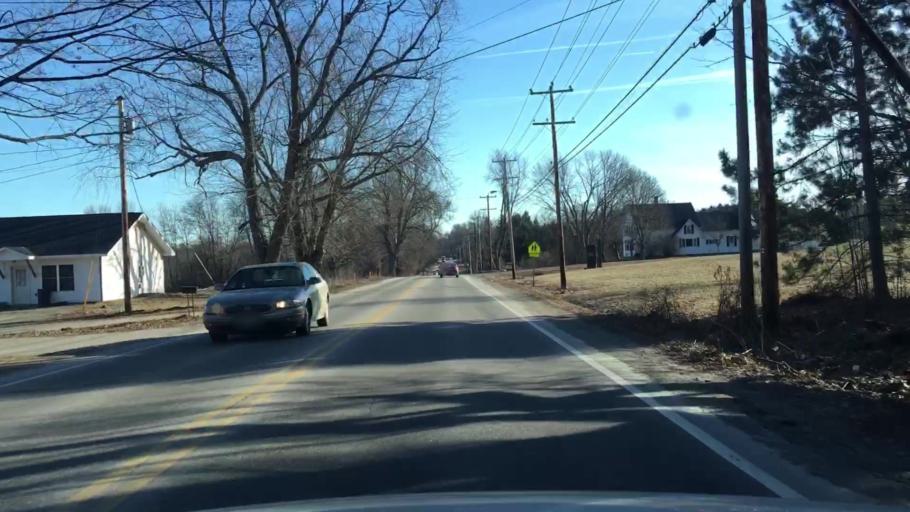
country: US
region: Maine
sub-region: Penobscot County
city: Bangor
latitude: 44.8184
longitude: -68.8016
